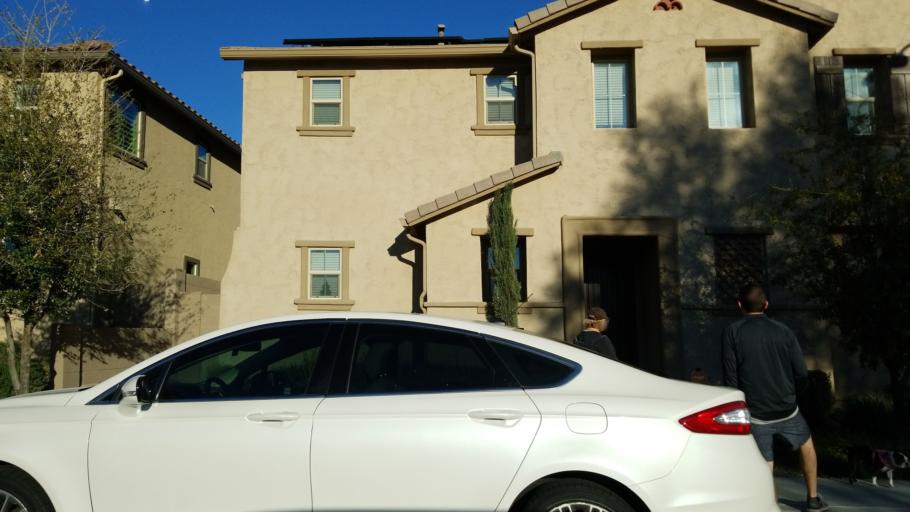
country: US
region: Arizona
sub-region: Maricopa County
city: Paradise Valley
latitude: 33.6280
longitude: -111.9800
